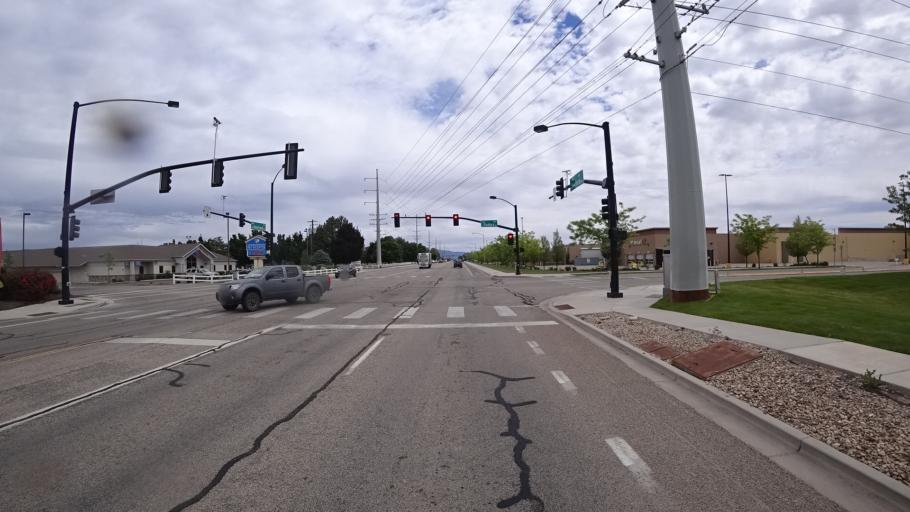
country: US
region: Idaho
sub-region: Ada County
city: Meridian
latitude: 43.5900
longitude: -116.4040
